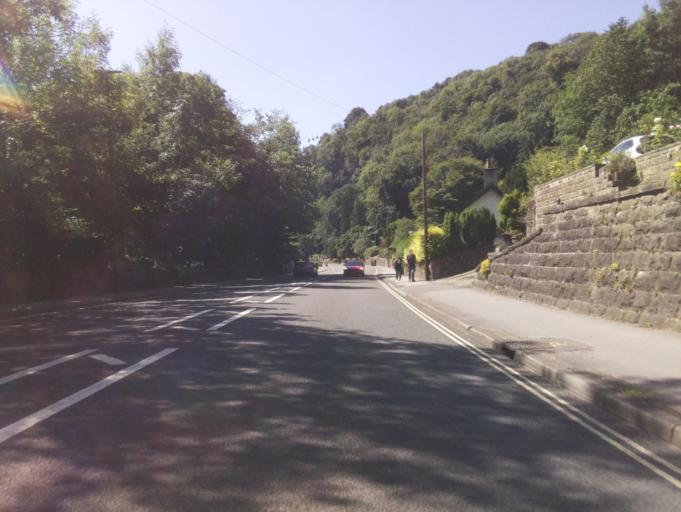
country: GB
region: England
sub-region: Derbyshire
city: Matlock
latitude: 53.1278
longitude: -1.5595
